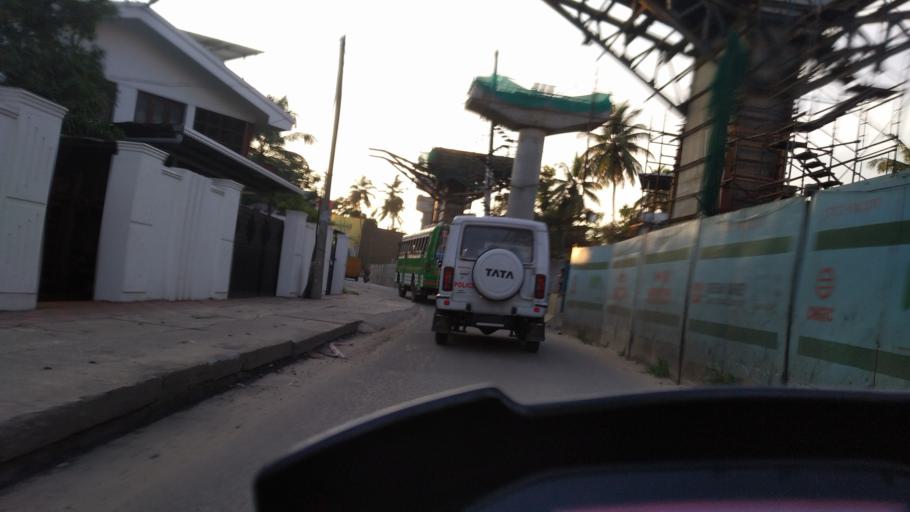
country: IN
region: Kerala
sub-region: Ernakulam
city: Cochin
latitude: 9.9522
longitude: 76.3303
